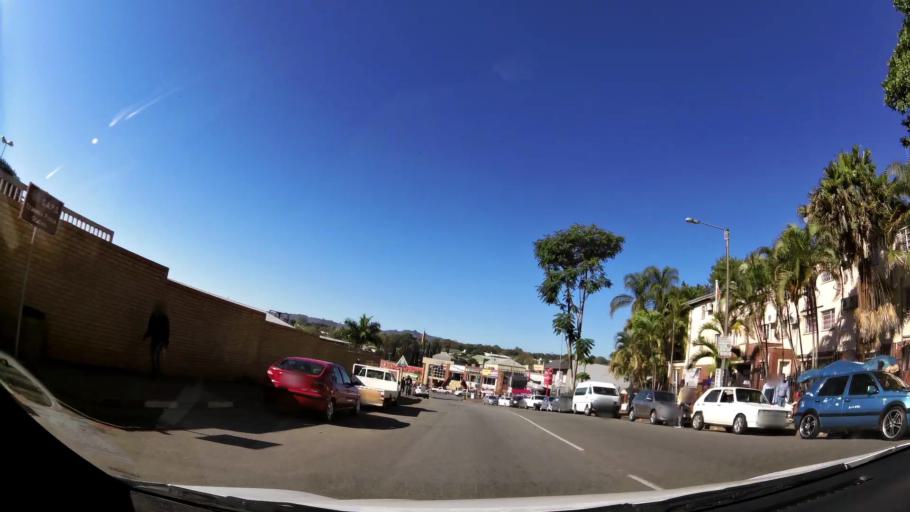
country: ZA
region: Limpopo
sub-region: Mopani District Municipality
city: Tzaneen
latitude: -23.8280
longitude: 30.1614
